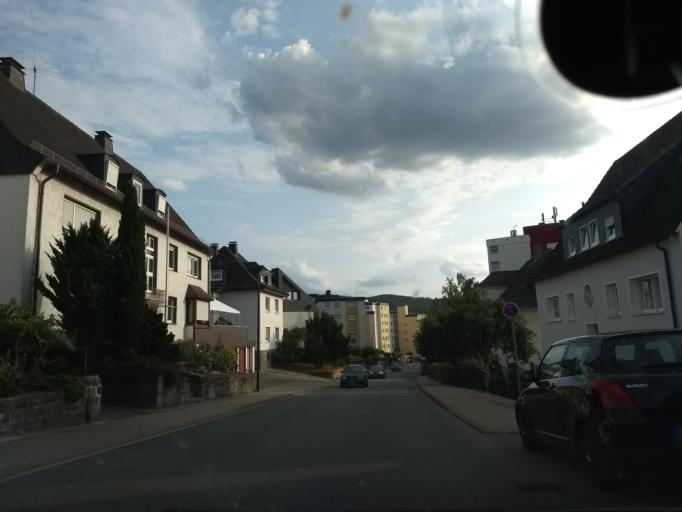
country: DE
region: North Rhine-Westphalia
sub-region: Regierungsbezirk Arnsberg
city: Arnsberg
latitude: 51.3871
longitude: 8.0779
